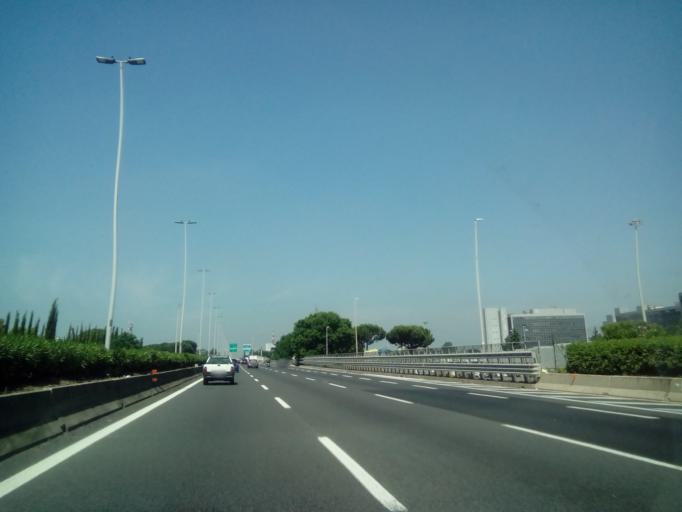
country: IT
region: Latium
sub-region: Citta metropolitana di Roma Capitale
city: Selcetta
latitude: 41.7969
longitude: 12.4869
